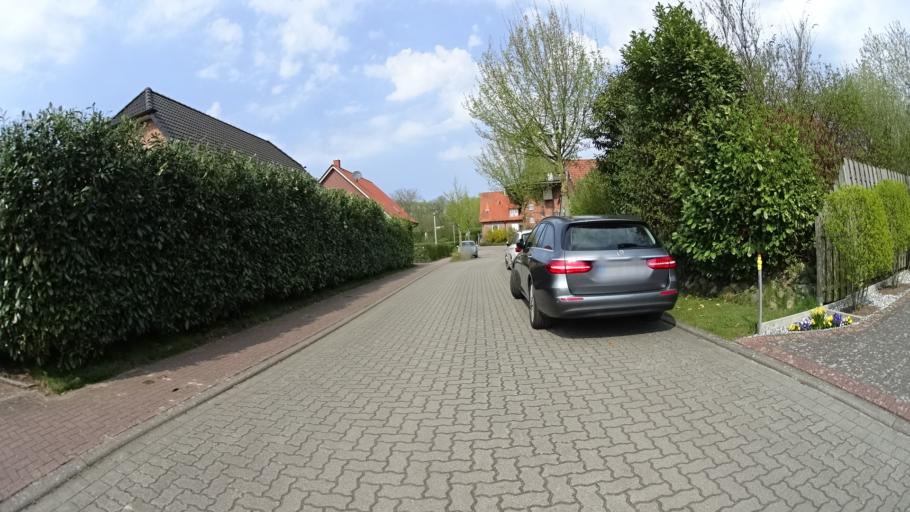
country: DE
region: Lower Saxony
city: Jork
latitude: 53.5389
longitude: 9.6925
